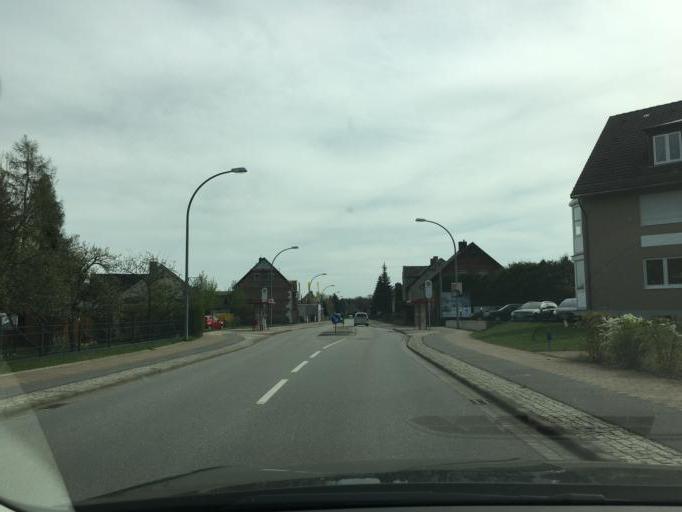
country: DE
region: Brandenburg
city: Spremberg
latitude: 51.5682
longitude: 14.3964
